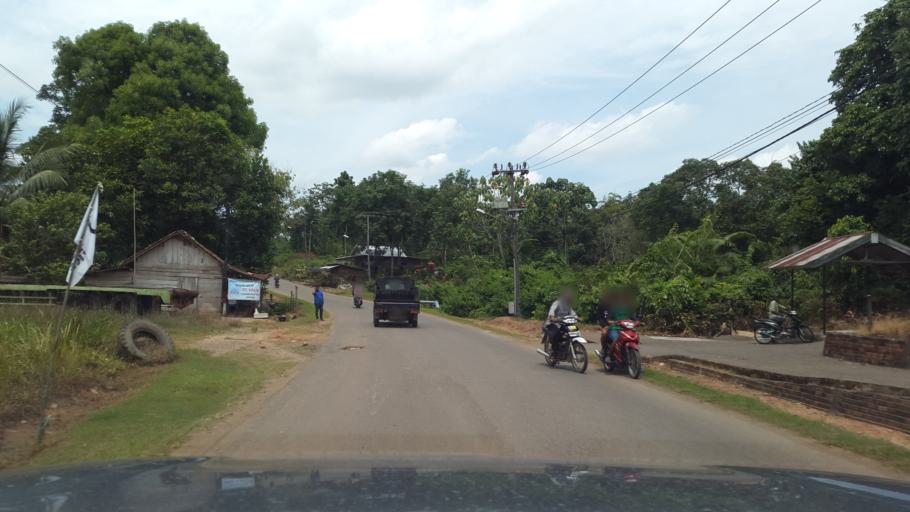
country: ID
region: South Sumatra
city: Gunungmegang Dalam
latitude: -3.2853
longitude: 103.8356
